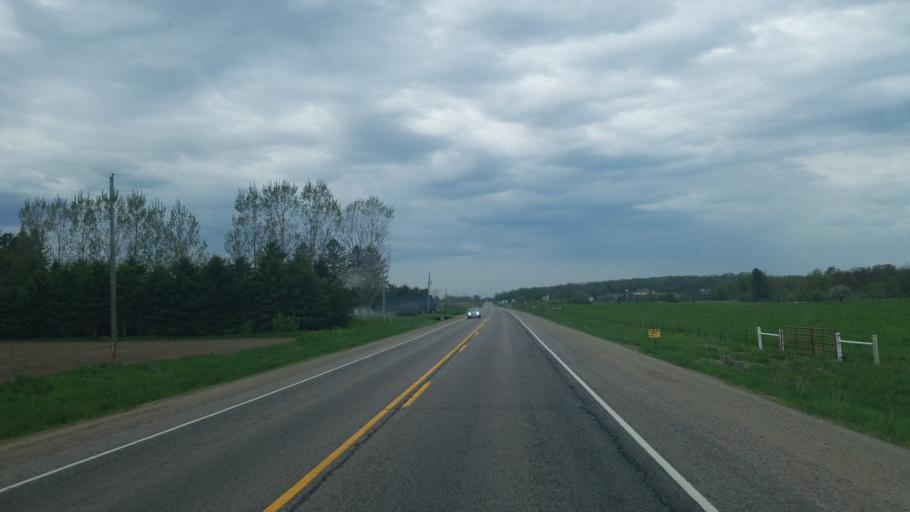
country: US
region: Wisconsin
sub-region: Marathon County
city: Spencer
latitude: 44.5986
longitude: -90.3245
